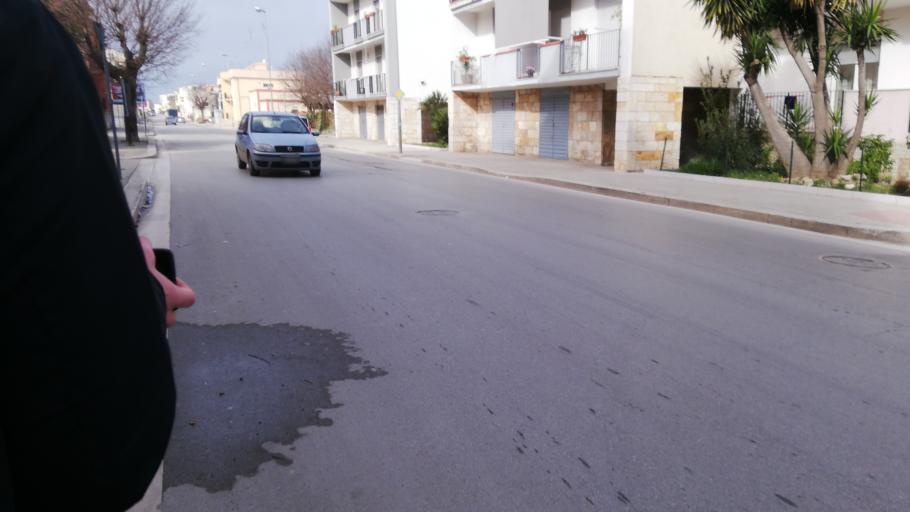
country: IT
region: Apulia
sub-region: Provincia di Barletta - Andria - Trani
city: Andria
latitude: 41.2385
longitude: 16.3001
